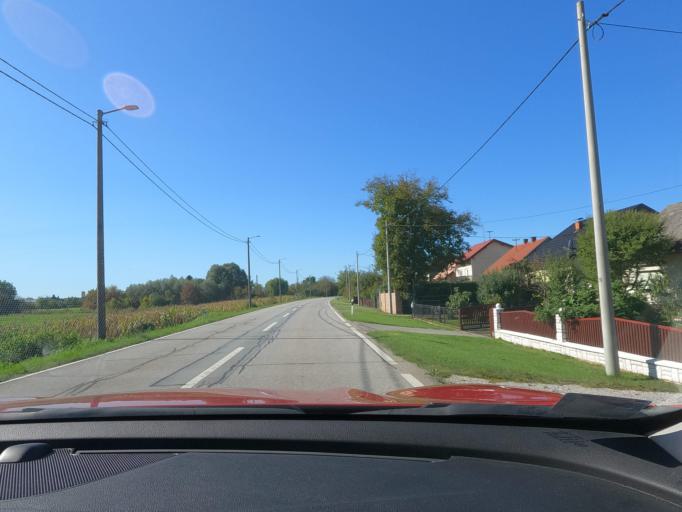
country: HR
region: Sisacko-Moslavacka
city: Budasevo
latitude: 45.4861
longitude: 16.4403
